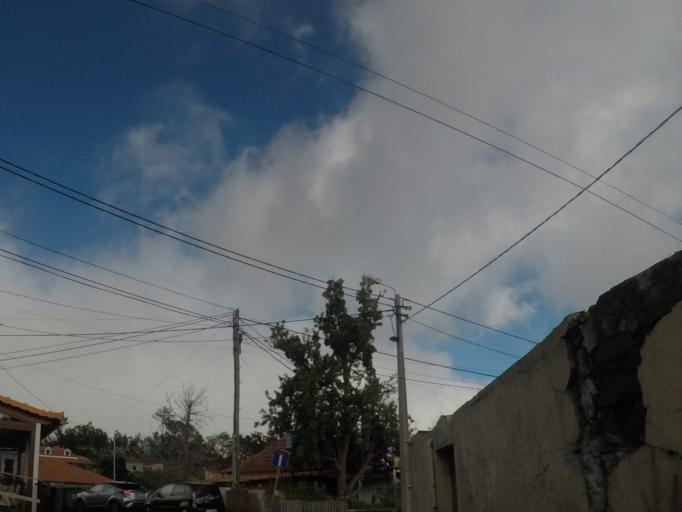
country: PT
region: Madeira
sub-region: Santa Cruz
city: Camacha
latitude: 32.6826
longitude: -16.8541
